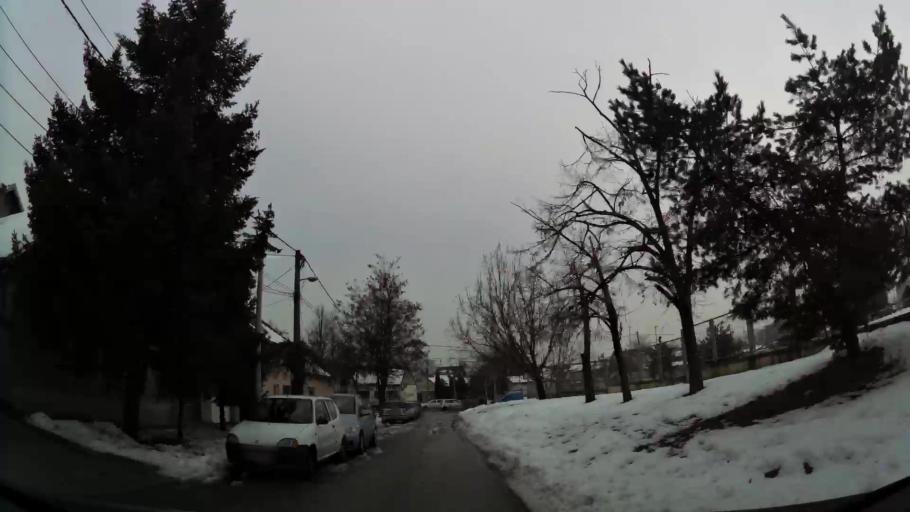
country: RS
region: Central Serbia
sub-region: Belgrade
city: Zemun
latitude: 44.8496
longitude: 20.3779
